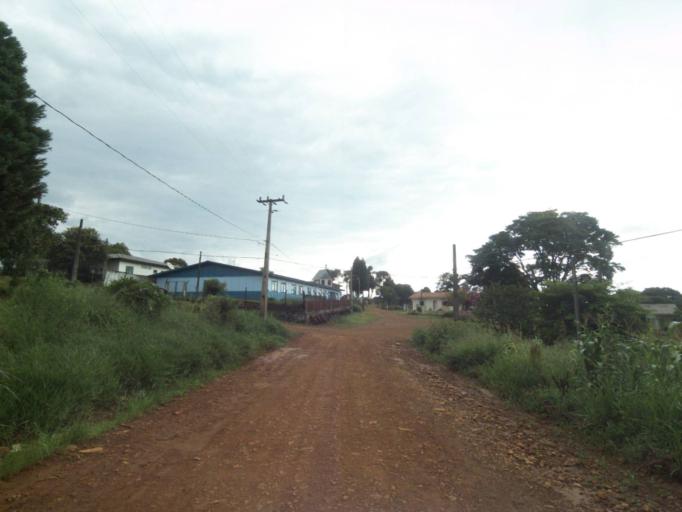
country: BR
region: Parana
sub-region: Pitanga
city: Pitanga
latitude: -24.8985
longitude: -51.9635
